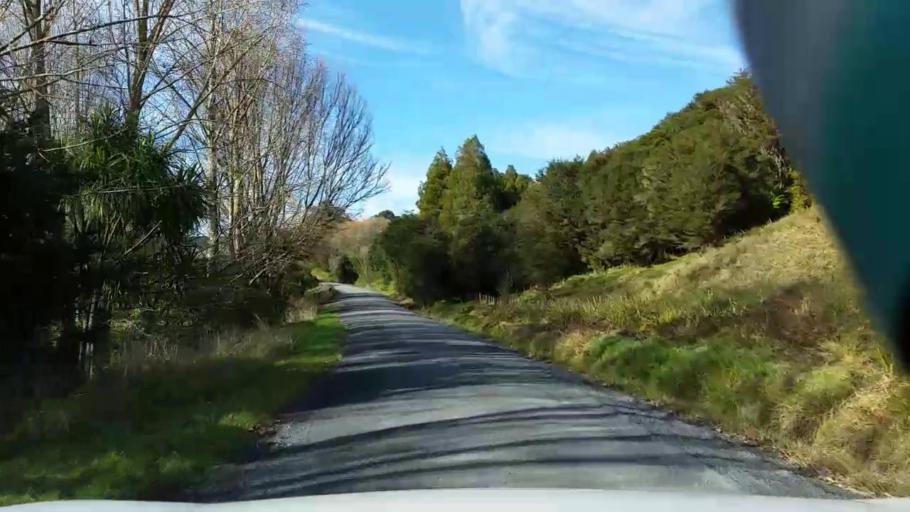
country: NZ
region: Waikato
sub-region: Hauraki District
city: Ngatea
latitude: -37.4669
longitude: 175.3983
